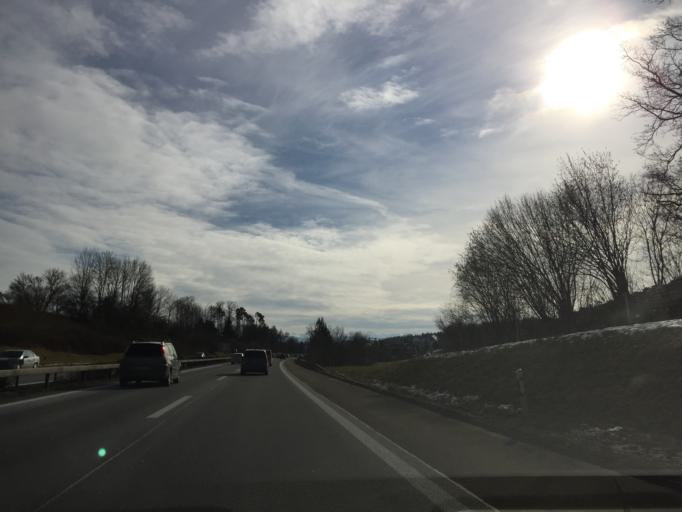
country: CH
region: Zurich
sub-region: Bezirk Horgen
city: Adliswil / Tal
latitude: 47.3150
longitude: 8.5394
